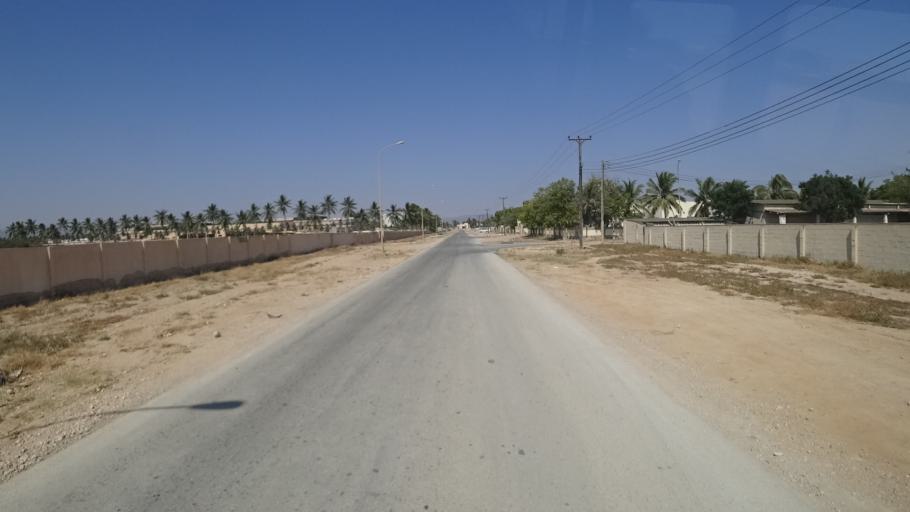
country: OM
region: Zufar
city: Salalah
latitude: 17.0289
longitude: 54.1666
